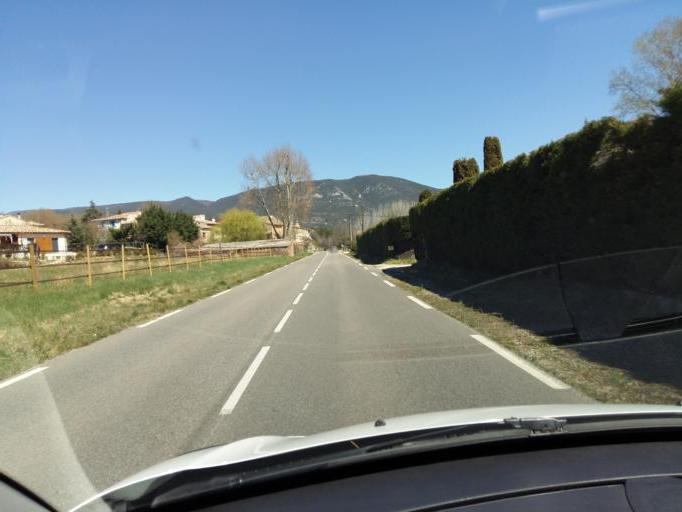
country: FR
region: Provence-Alpes-Cote d'Azur
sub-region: Departement du Vaucluse
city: Apt
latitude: 43.9071
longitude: 5.4375
